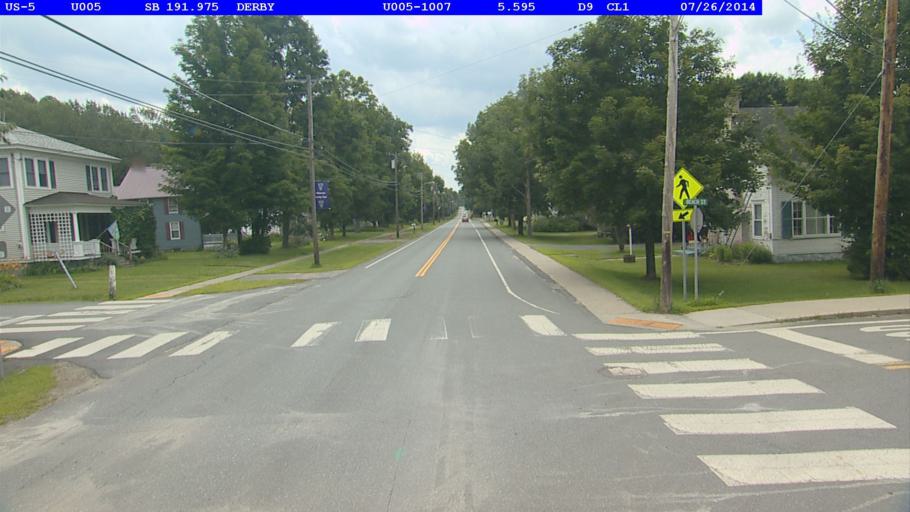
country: US
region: Vermont
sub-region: Orleans County
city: Newport
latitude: 45.0014
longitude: -72.1023
